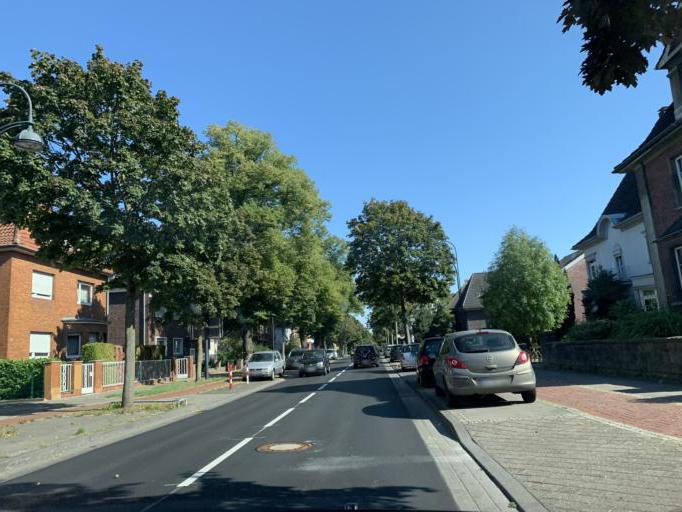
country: DE
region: North Rhine-Westphalia
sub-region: Regierungsbezirk Arnsberg
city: Hamm
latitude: 51.6881
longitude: 7.8429
